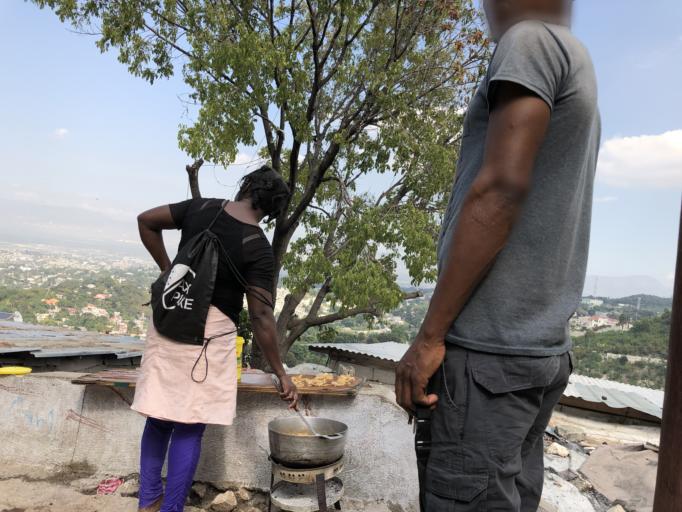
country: HT
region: Ouest
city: Port-au-Prince
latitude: 18.5217
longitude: -72.3176
